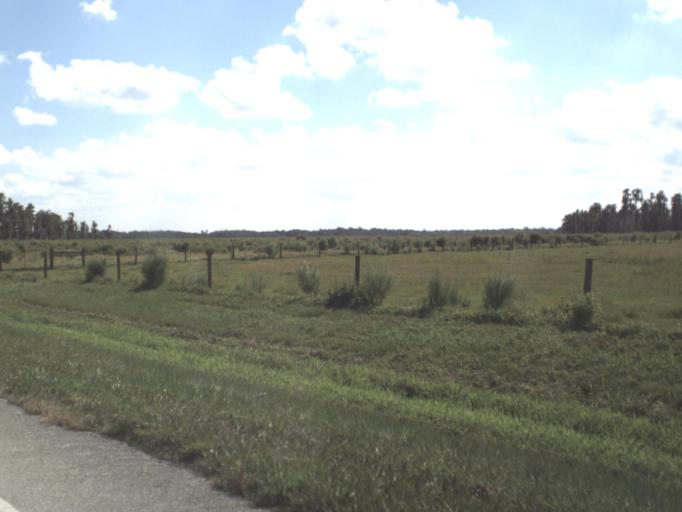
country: US
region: Florida
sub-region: Hardee County
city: Zolfo Springs
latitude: 27.4445
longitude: -81.6204
